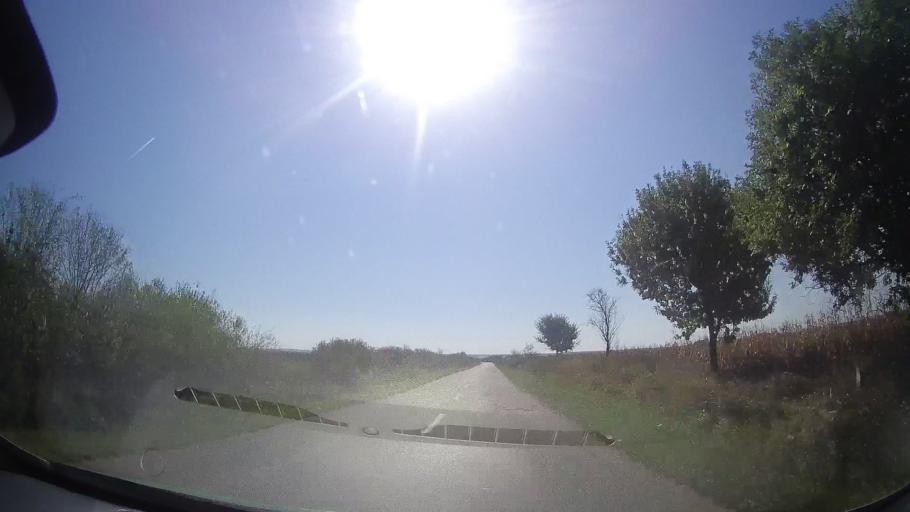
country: RO
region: Timis
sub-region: Comuna Bethausen
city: Bethausen
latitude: 45.8252
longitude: 21.9596
